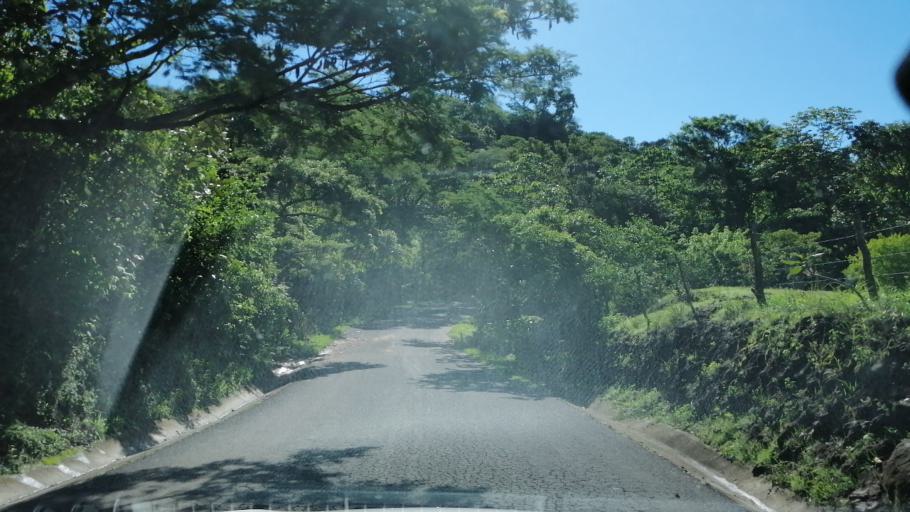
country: SV
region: Morazan
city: Corinto
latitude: 13.8121
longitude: -87.9848
